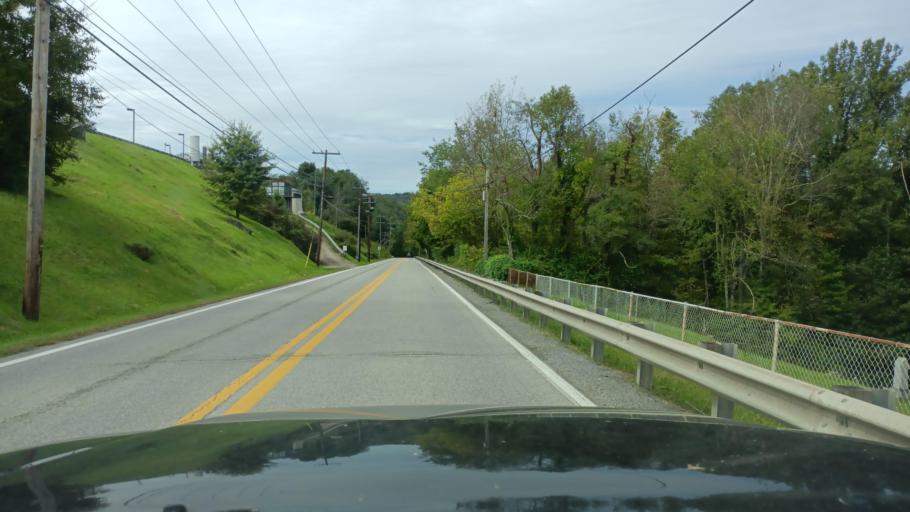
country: US
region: West Virginia
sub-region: Taylor County
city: Grafton
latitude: 39.3443
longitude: -80.0243
